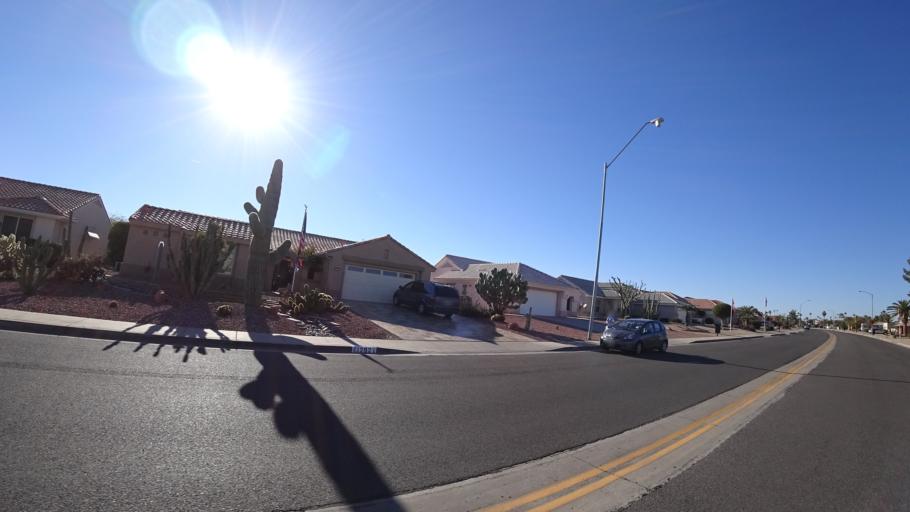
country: US
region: Arizona
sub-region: Maricopa County
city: Sun City West
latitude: 33.6692
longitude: -112.3420
